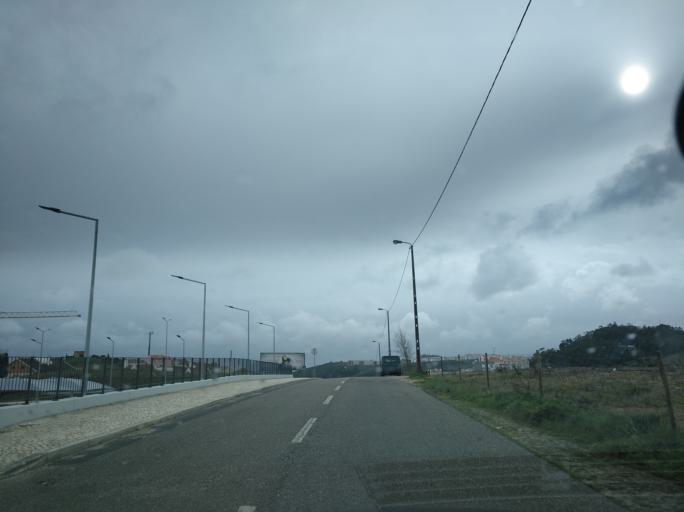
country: PT
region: Lisbon
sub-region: Odivelas
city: Canecas
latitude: 38.7973
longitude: -9.2299
